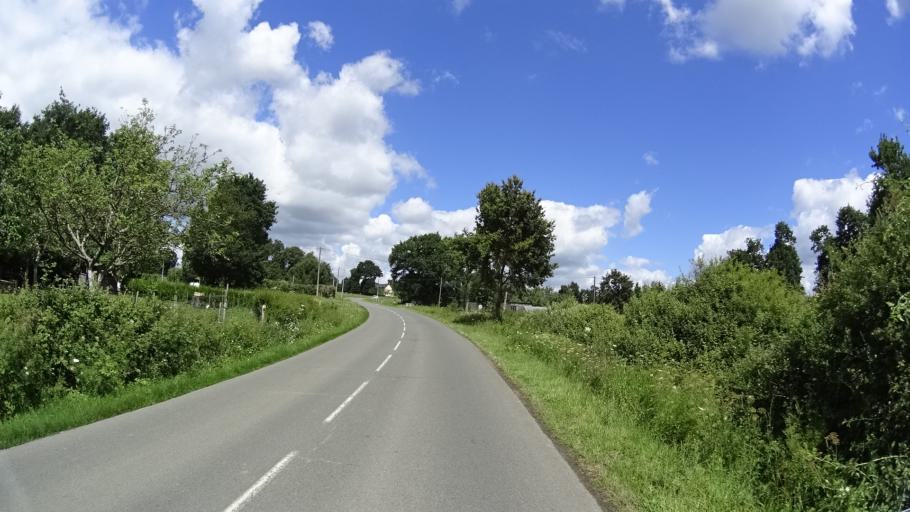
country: FR
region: Brittany
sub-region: Departement d'Ille-et-Vilaine
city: Saint-Gilles
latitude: 48.1367
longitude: -1.8259
